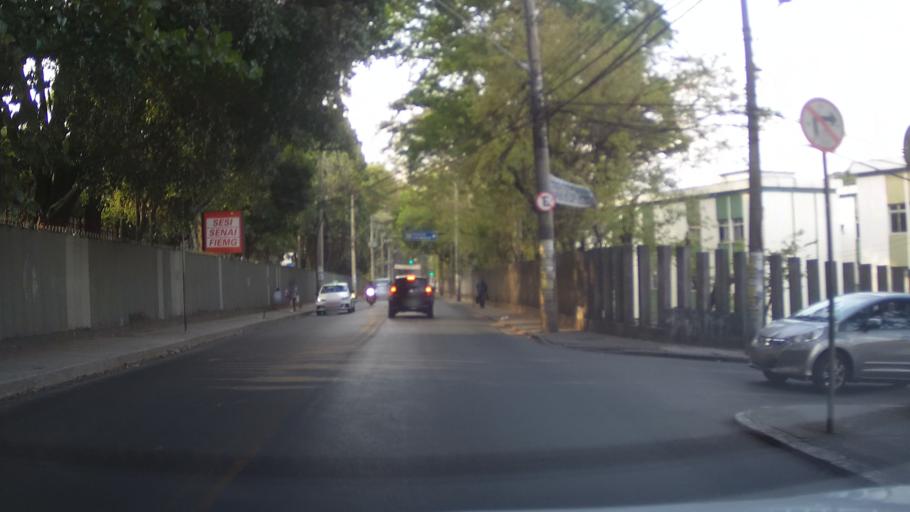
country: BR
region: Minas Gerais
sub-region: Belo Horizonte
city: Belo Horizonte
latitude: -19.8970
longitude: -43.9118
